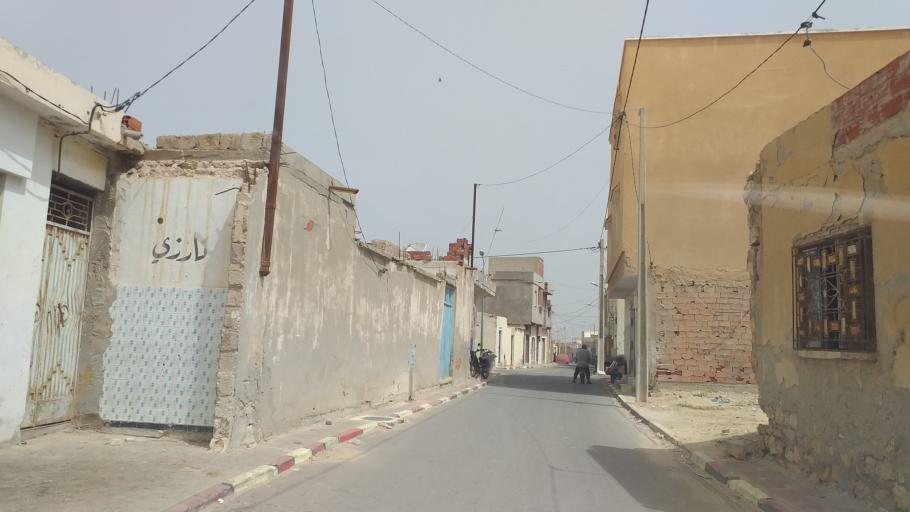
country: TN
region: Qabis
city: Gabes
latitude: 33.9400
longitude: 10.0634
